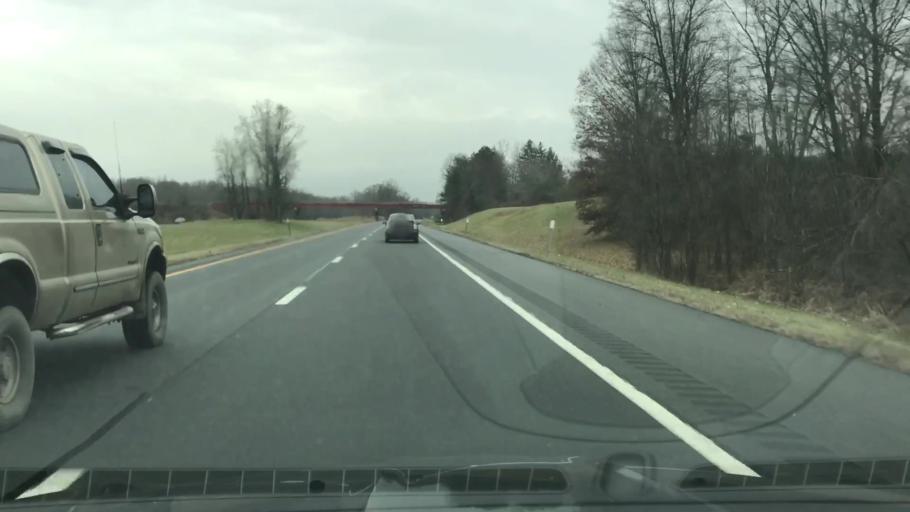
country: US
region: New York
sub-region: Orange County
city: Montgomery
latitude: 41.4860
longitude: -74.2812
